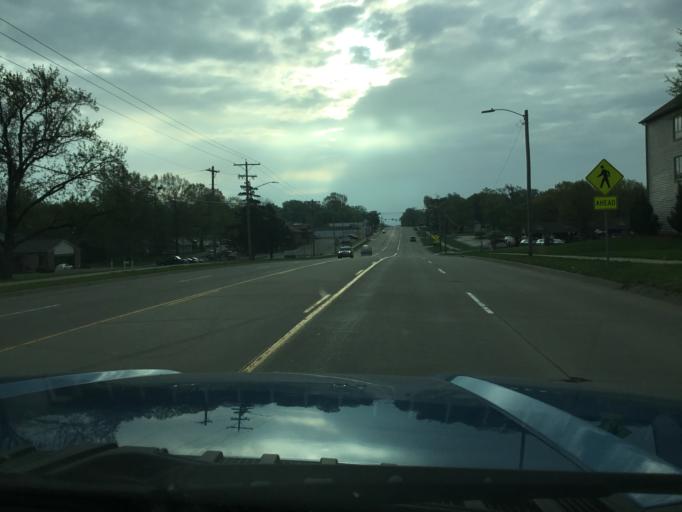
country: US
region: Kansas
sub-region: Shawnee County
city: Topeka
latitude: 39.0585
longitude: -95.7210
